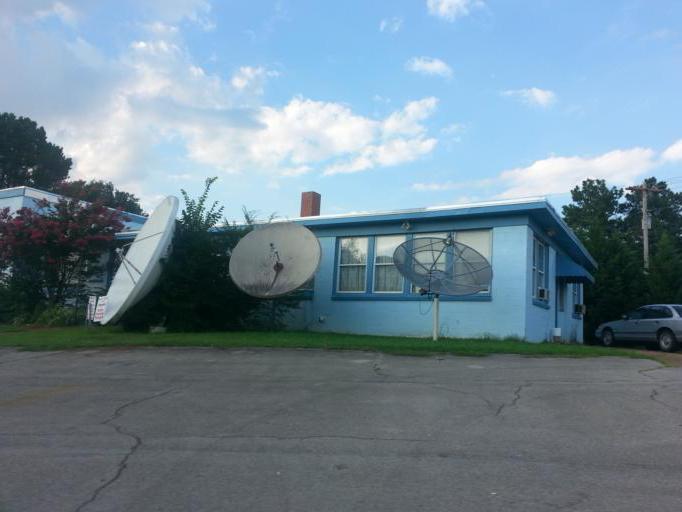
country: US
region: Tennessee
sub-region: Blount County
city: Eagleton Village
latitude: 35.7940
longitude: -83.9445
